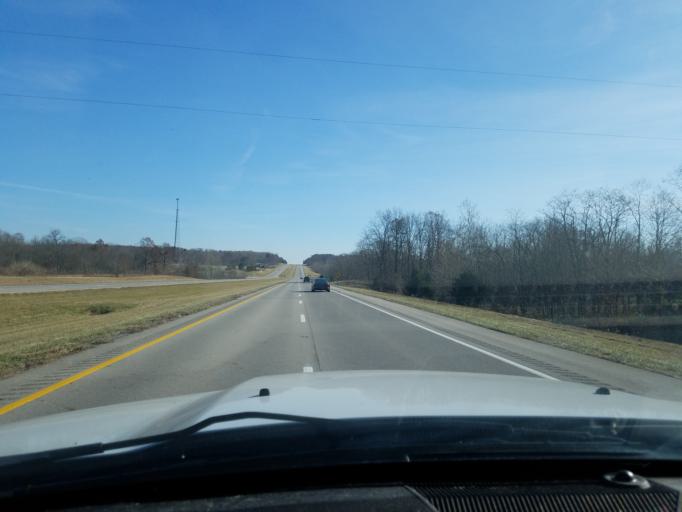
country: US
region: Ohio
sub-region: Adams County
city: Winchester
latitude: 38.9340
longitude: -83.6251
